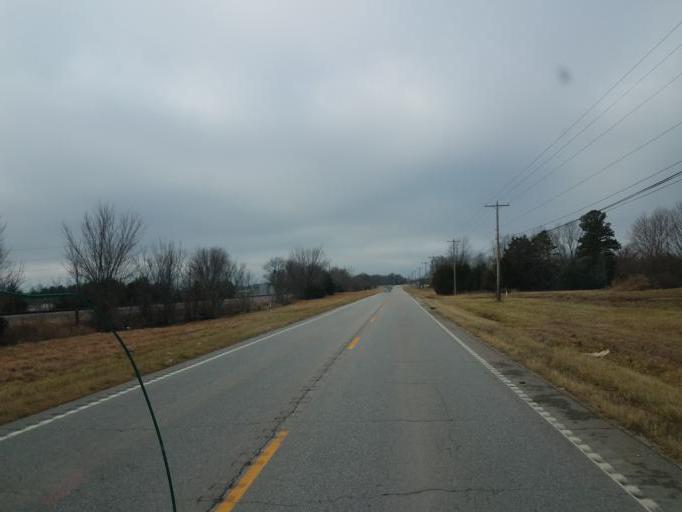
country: US
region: Missouri
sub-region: Greene County
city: Strafford
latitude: 37.2502
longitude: -93.1709
